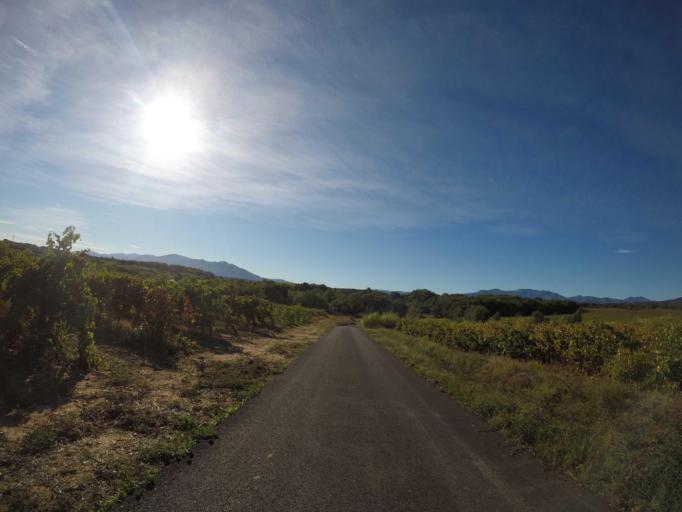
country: FR
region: Languedoc-Roussillon
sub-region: Departement des Pyrenees-Orientales
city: Trouillas
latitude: 42.5767
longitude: 2.7852
